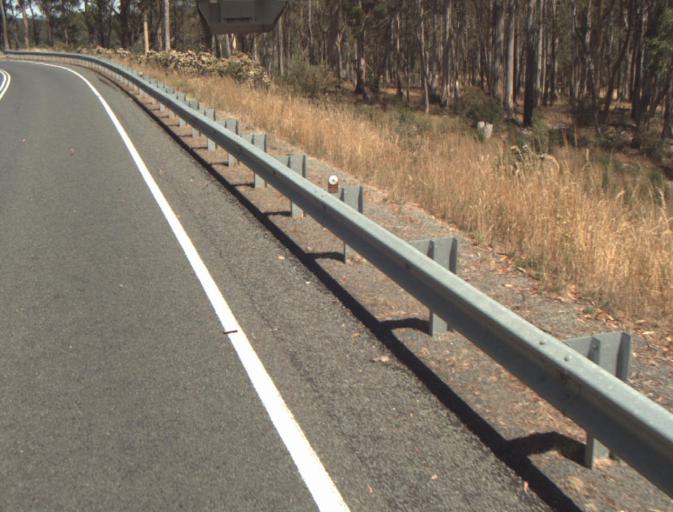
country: AU
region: Tasmania
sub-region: Launceston
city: Newstead
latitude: -41.3442
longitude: 147.3434
